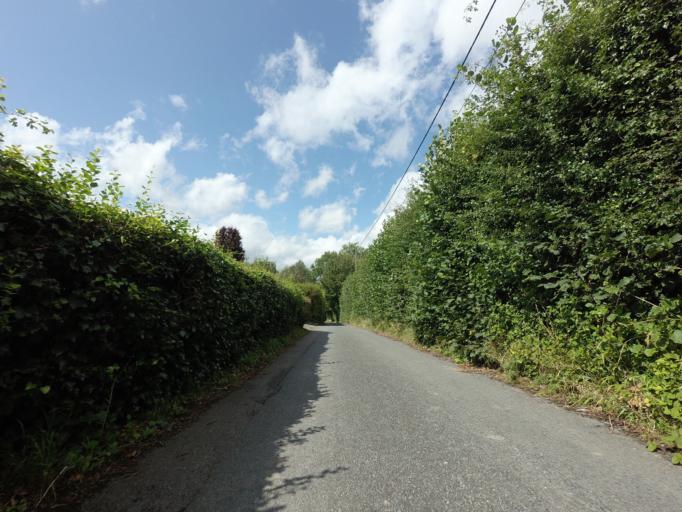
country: GB
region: England
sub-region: Kent
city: Borough Green
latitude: 51.2654
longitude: 0.2931
